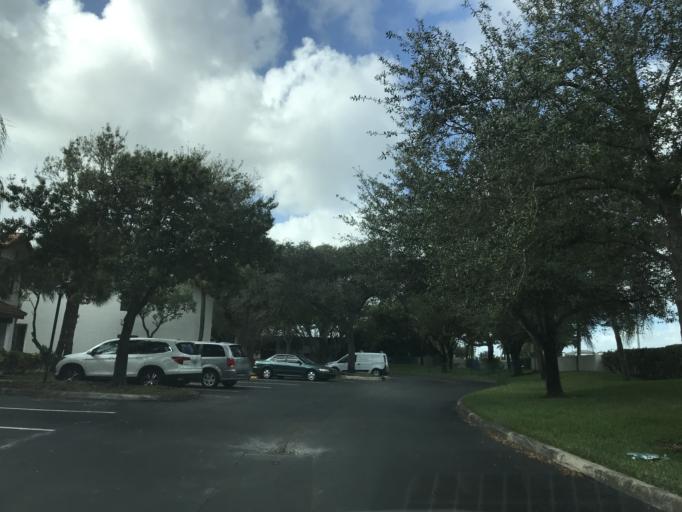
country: US
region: Florida
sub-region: Broward County
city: Coconut Creek
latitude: 26.2735
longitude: -80.1876
